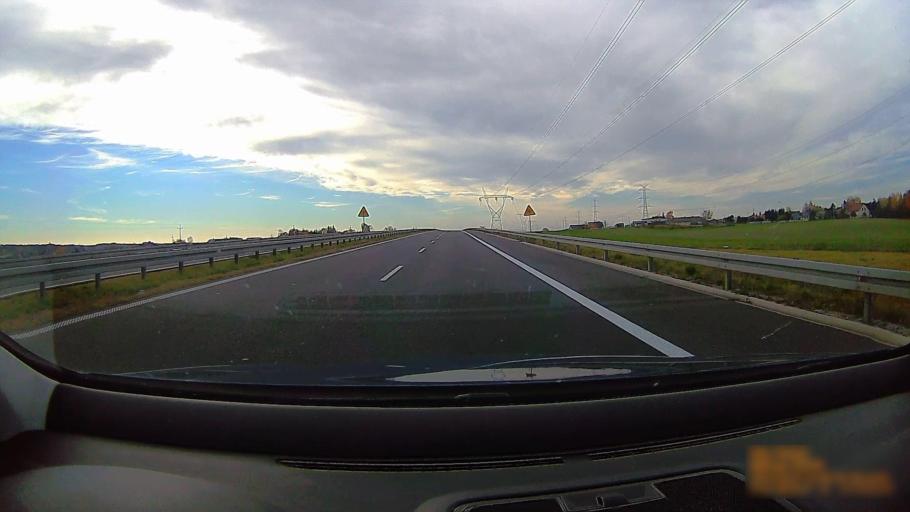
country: PL
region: Greater Poland Voivodeship
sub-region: Powiat ostrowski
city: Przygodzice
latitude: 51.6085
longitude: 17.8558
